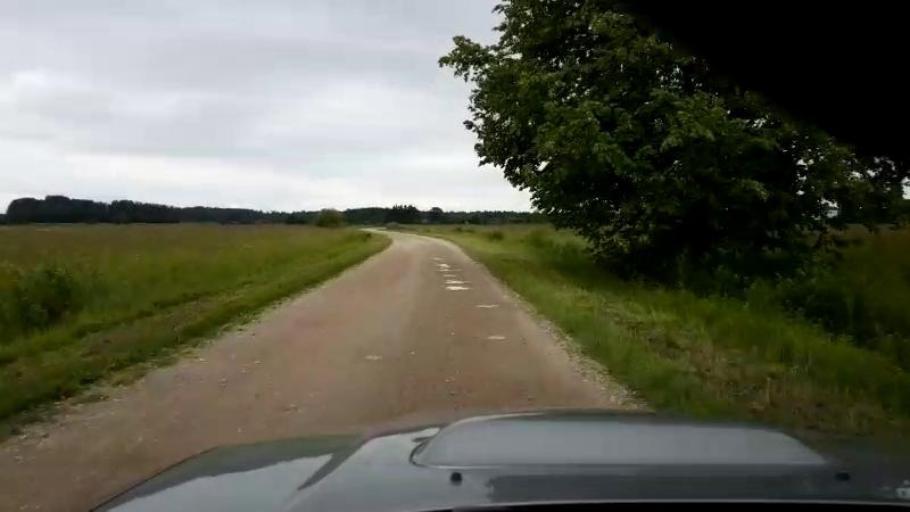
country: EE
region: Paernumaa
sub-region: Halinga vald
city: Parnu-Jaagupi
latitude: 58.5356
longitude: 24.5606
